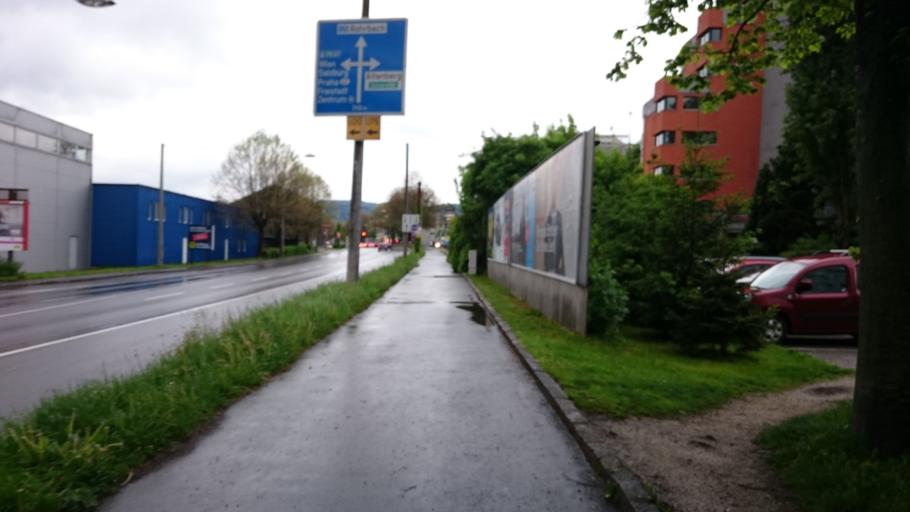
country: AT
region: Upper Austria
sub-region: Linz Stadt
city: Linz
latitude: 48.3288
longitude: 14.3217
